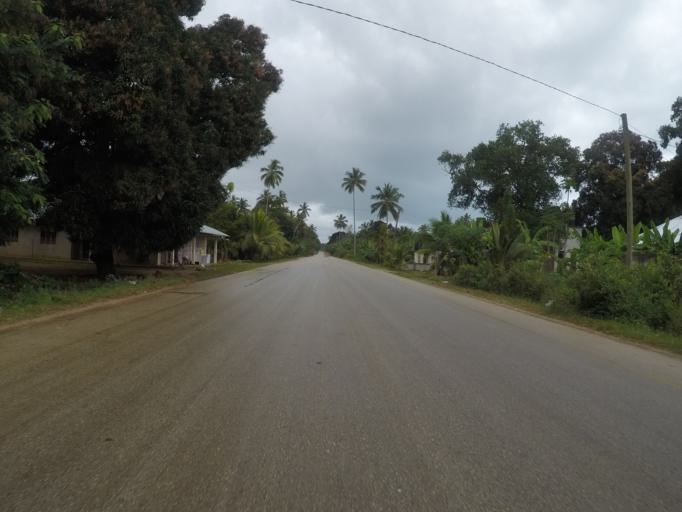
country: TZ
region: Zanzibar North
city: Mkokotoni
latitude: -5.9905
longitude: 39.1959
